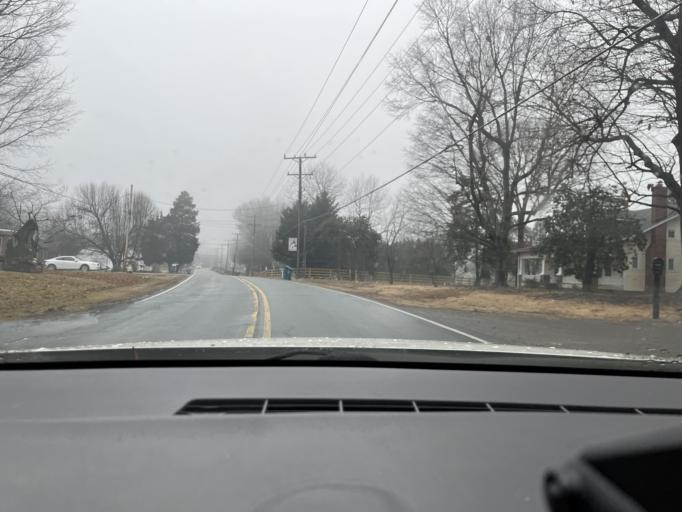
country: US
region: North Carolina
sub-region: Guilford County
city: Pleasant Garden
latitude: 35.9721
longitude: -79.7661
